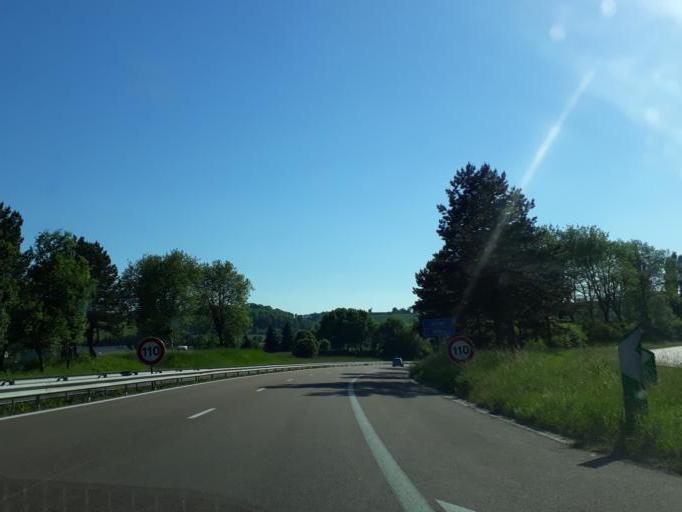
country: FR
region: Bourgogne
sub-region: Departement de la Cote-d'Or
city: Pouilly-en-Auxois
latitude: 47.2537
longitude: 4.5695
